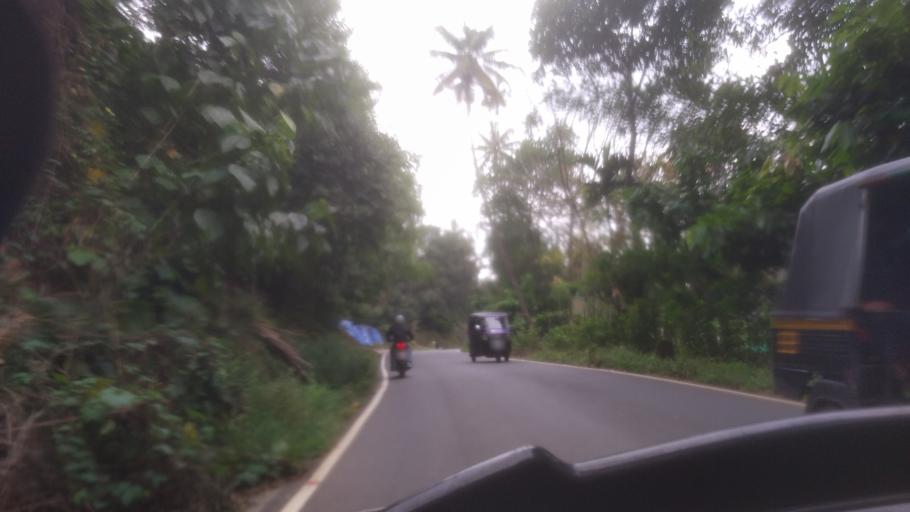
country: IN
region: Kerala
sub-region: Idukki
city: Idukki
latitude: 9.9620
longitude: 77.0041
